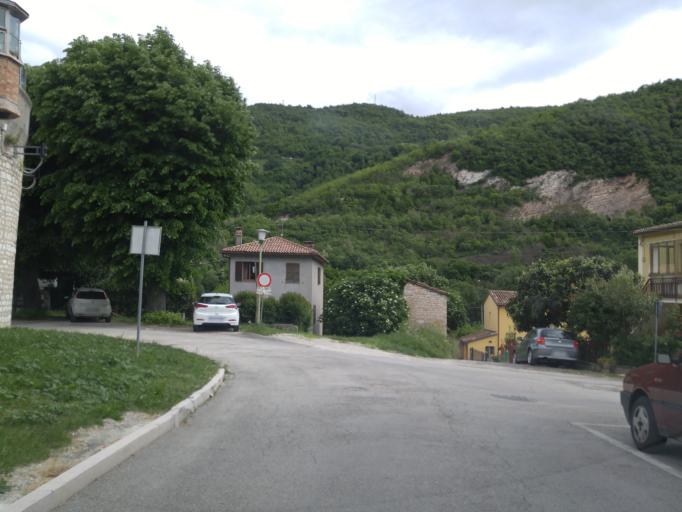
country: IT
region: The Marches
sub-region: Provincia di Pesaro e Urbino
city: Fossombrone
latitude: 43.6860
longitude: 12.8114
